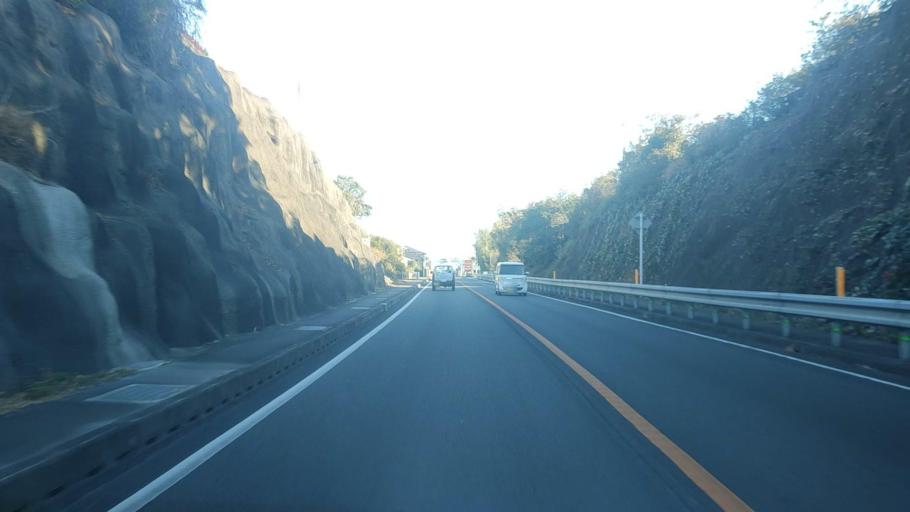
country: JP
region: Miyazaki
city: Nobeoka
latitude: 32.3674
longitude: 131.6271
